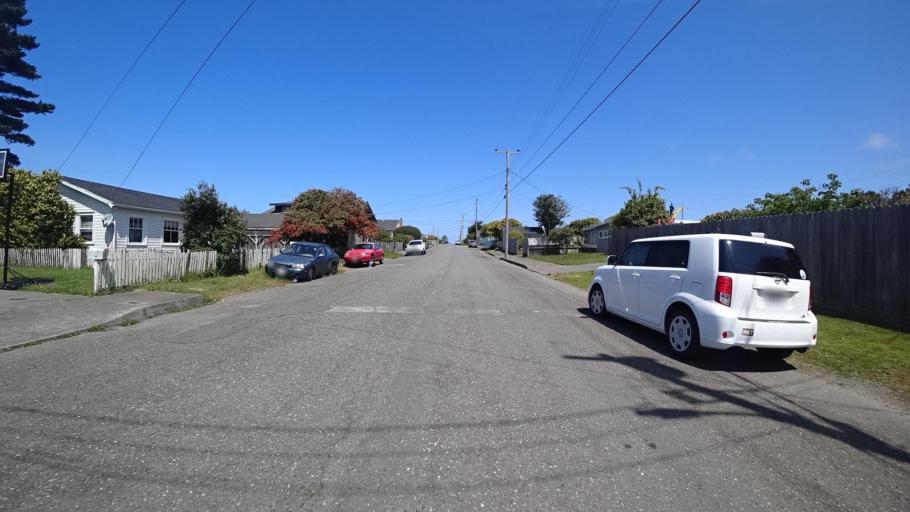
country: US
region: California
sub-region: Humboldt County
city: Bayview
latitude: 40.7758
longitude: -124.1726
